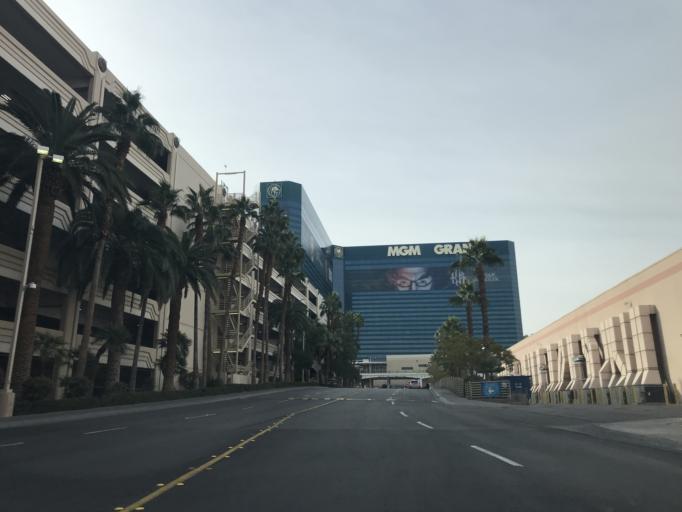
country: US
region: Nevada
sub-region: Clark County
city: Paradise
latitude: 36.1030
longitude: -115.1656
